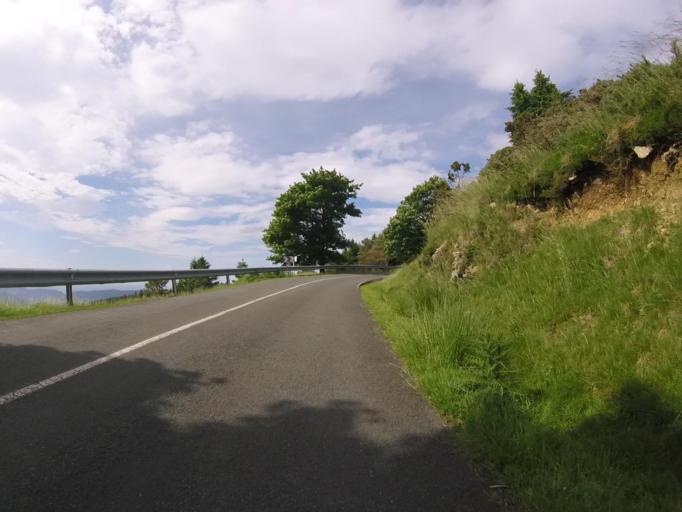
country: ES
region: Navarre
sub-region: Provincia de Navarra
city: Goizueta
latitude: 43.2458
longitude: -1.8257
